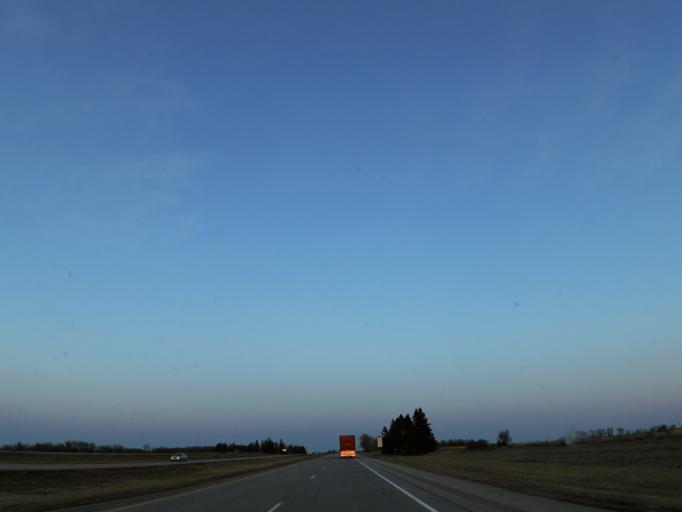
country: US
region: Minnesota
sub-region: Mower County
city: Austin
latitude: 43.6734
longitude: -92.7838
